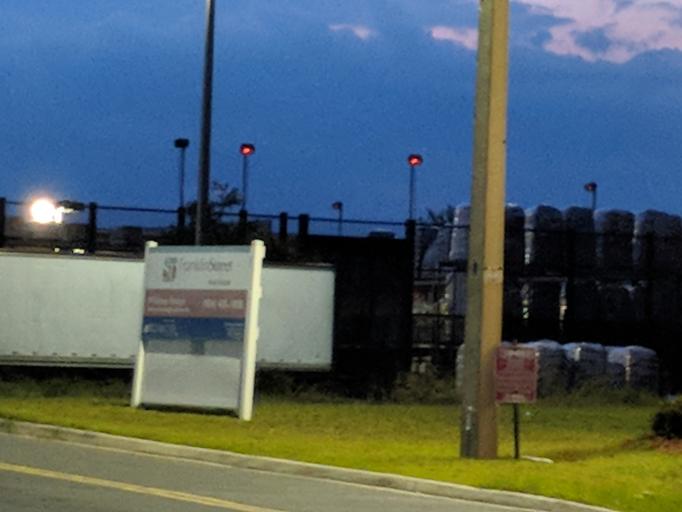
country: US
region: Florida
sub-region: Nassau County
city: Yulee
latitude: 30.6283
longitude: -81.5469
